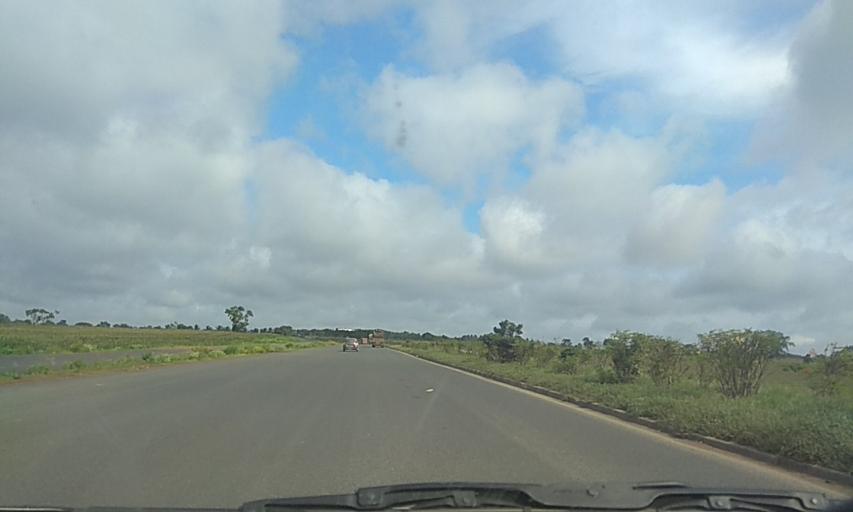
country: IN
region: Karnataka
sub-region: Haveri
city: Shiggaon
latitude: 15.0018
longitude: 75.2062
